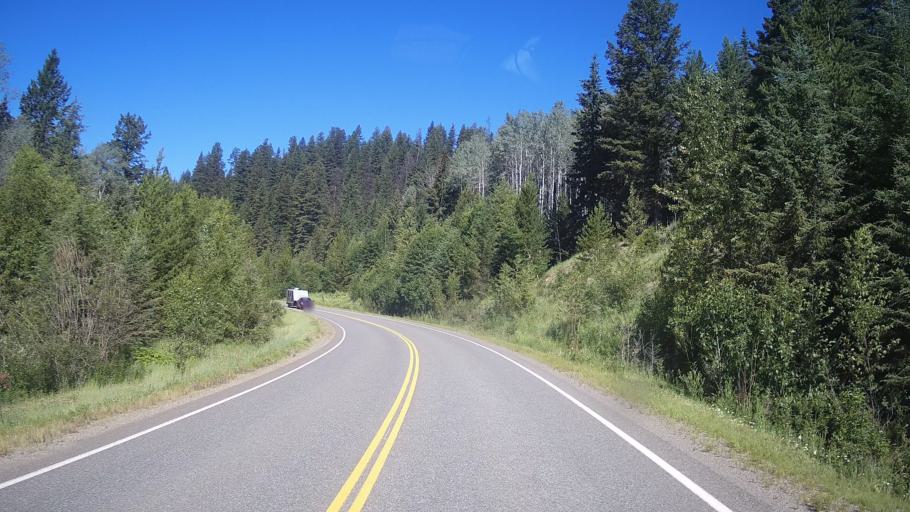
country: CA
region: British Columbia
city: Kamloops
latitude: 51.4732
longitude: -120.5410
